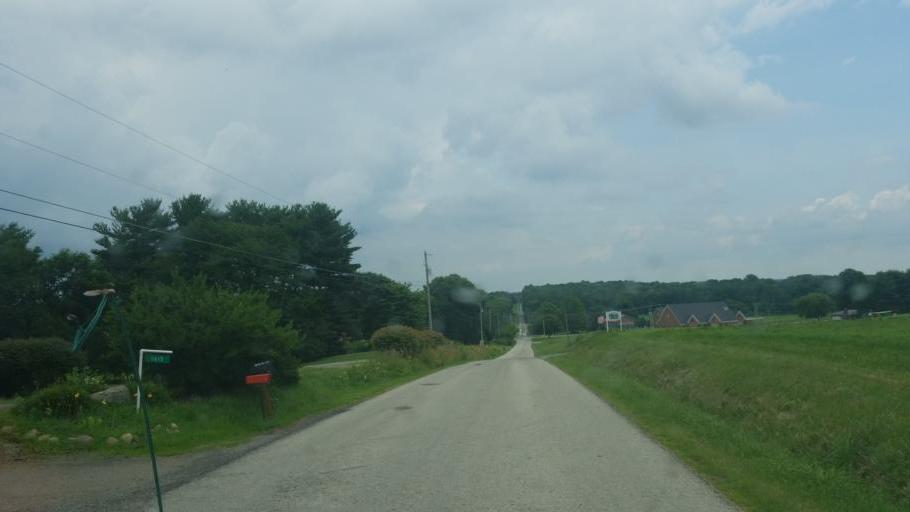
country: US
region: Ohio
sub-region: Wayne County
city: Wooster
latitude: 40.8872
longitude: -81.9736
